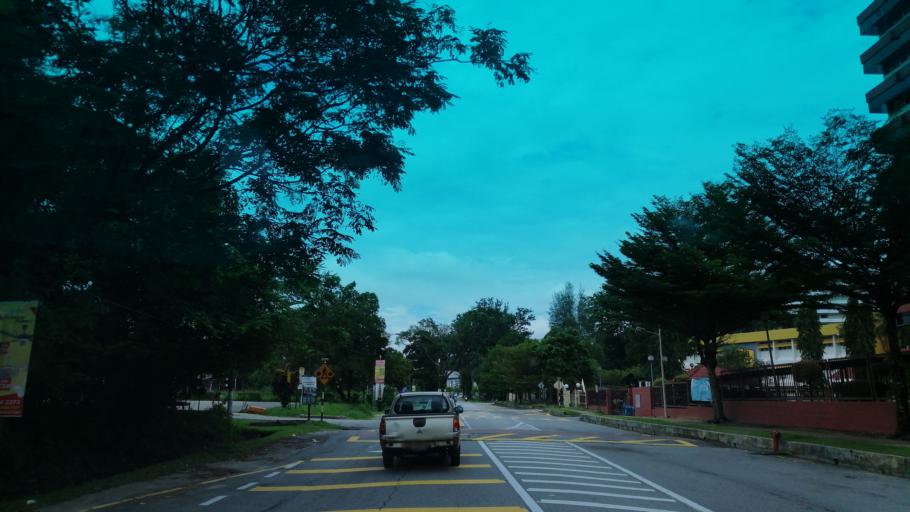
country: MY
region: Perak
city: Taiping
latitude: 4.8568
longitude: 100.7396
